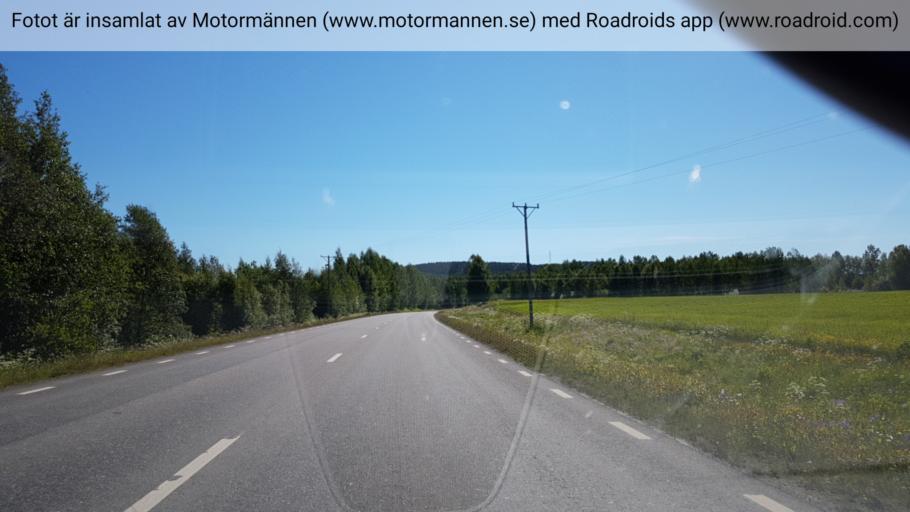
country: SE
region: Norrbotten
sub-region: Bodens Kommun
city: Boden
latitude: 65.8508
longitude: 21.5743
